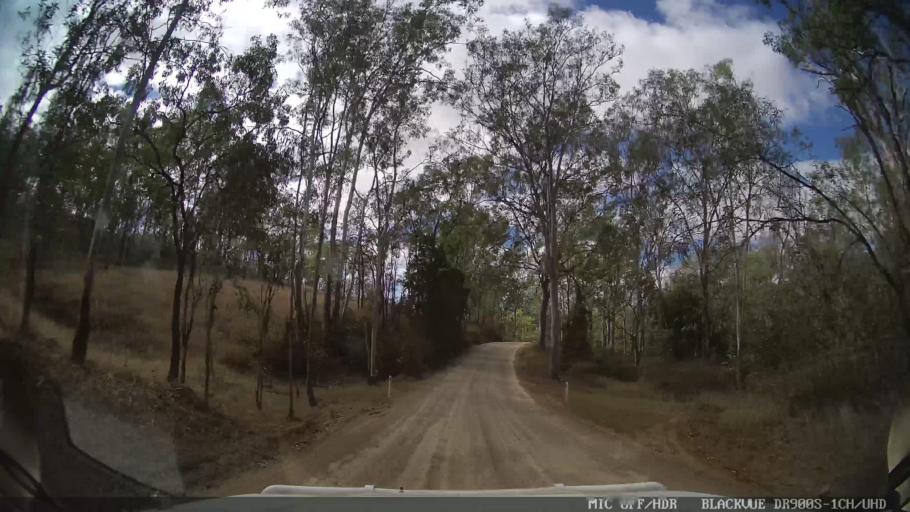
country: AU
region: Queensland
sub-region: Gladstone
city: Toolooa
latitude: -24.5520
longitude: 151.3372
